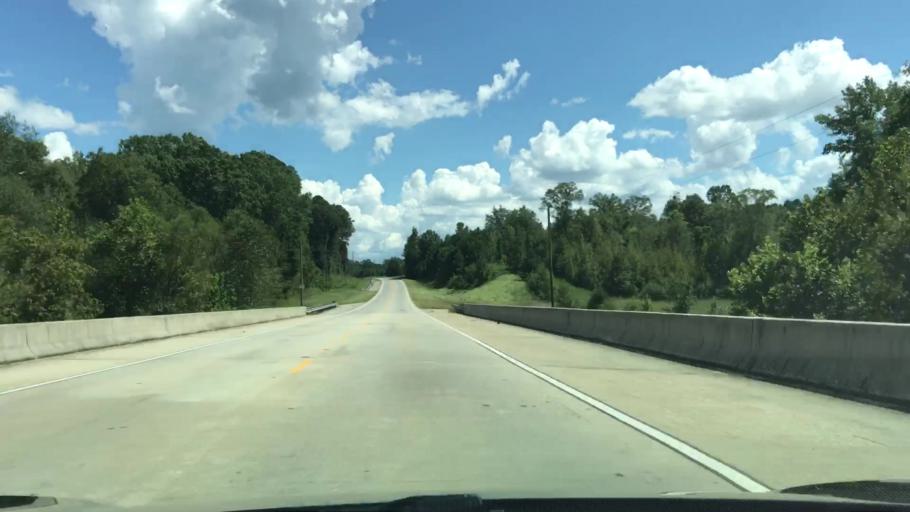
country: US
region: Georgia
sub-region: Greene County
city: Greensboro
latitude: 33.6702
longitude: -83.2611
